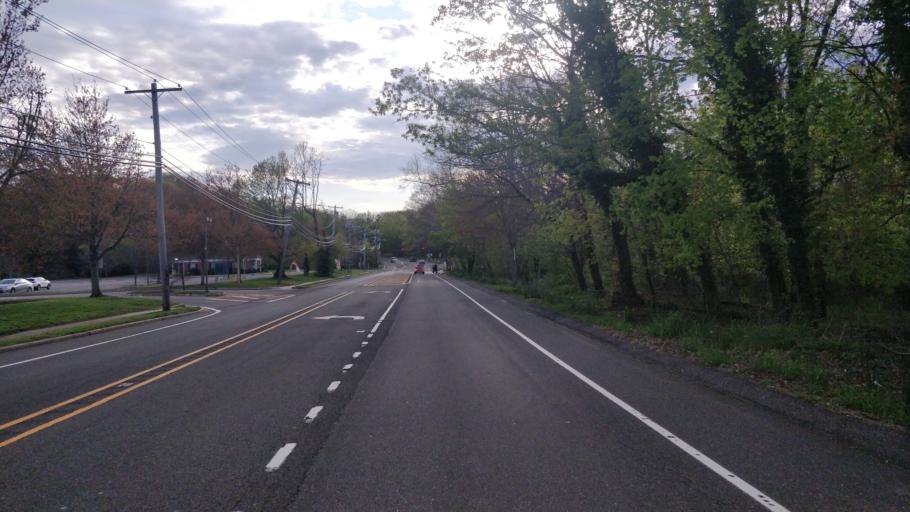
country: US
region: New York
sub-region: Suffolk County
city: Fort Salonga
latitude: 40.9125
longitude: -73.2983
